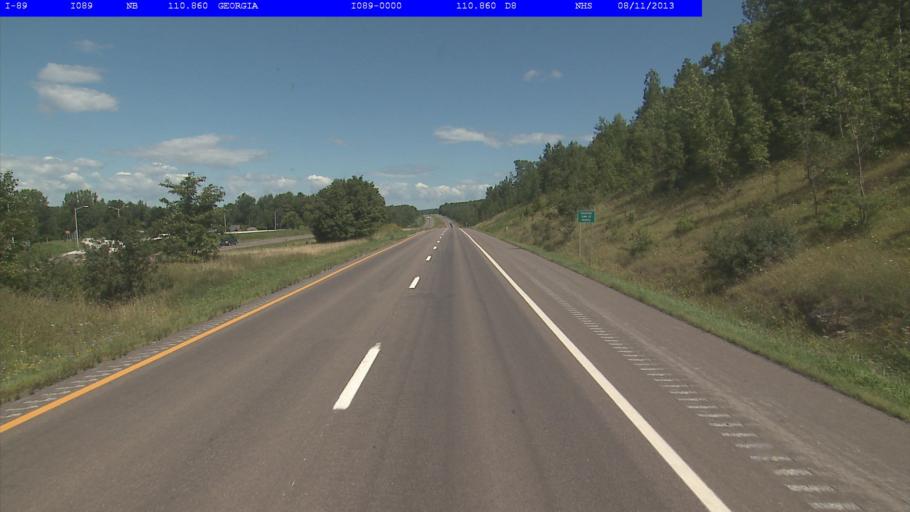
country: US
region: Vermont
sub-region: Franklin County
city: Saint Albans
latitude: 44.7534
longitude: -73.0775
